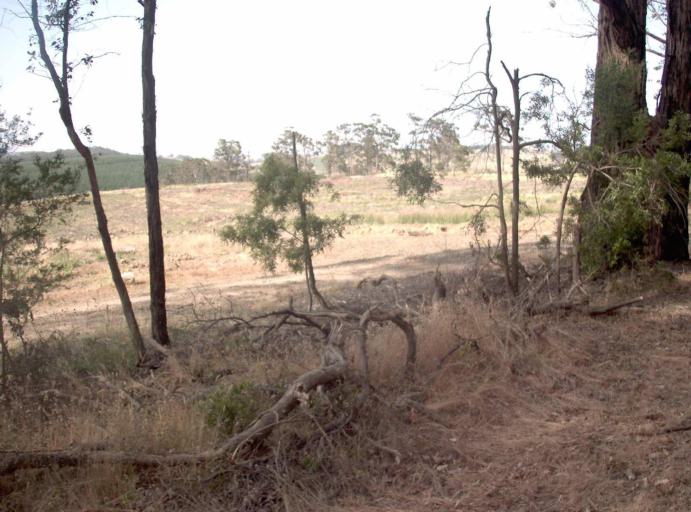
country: AU
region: Victoria
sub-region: Latrobe
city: Moe
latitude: -38.2845
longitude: 146.2578
